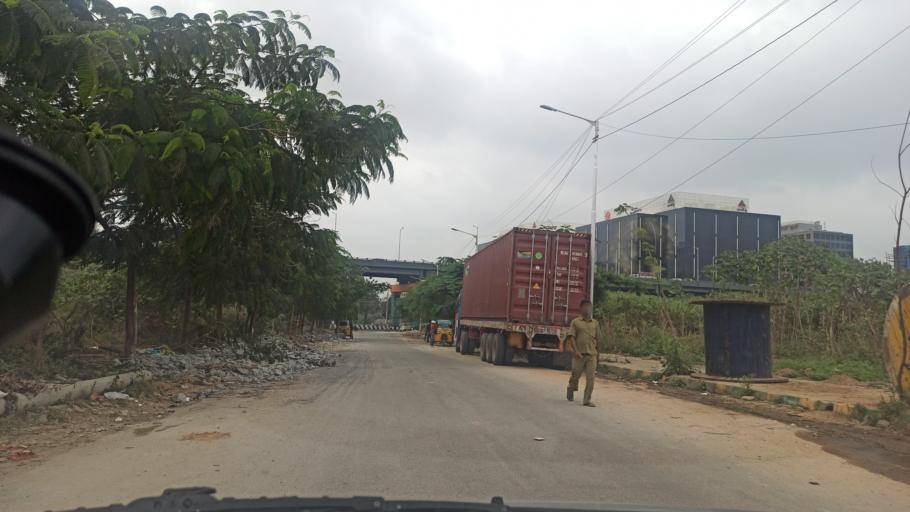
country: IN
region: Karnataka
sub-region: Bangalore Urban
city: Yelahanka
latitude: 13.0397
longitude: 77.6178
